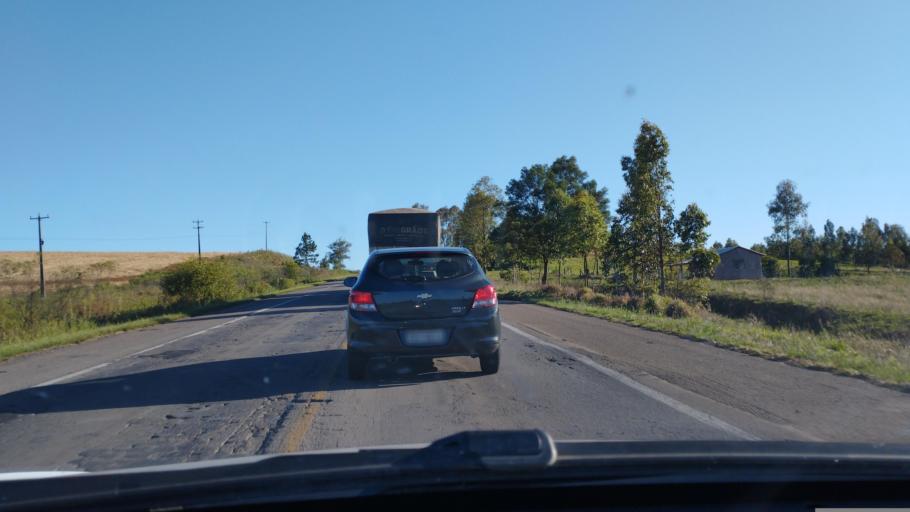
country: BR
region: Rio Grande do Sul
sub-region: Julio De Castilhos
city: Julio de Castilhos
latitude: -29.3746
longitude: -53.6709
